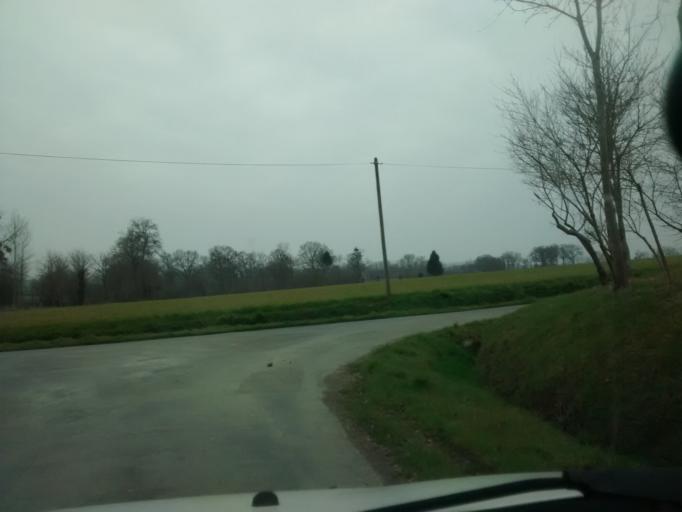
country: FR
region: Brittany
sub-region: Departement d'Ille-et-Vilaine
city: Bazouges-la-Perouse
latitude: 48.4003
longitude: -1.5893
